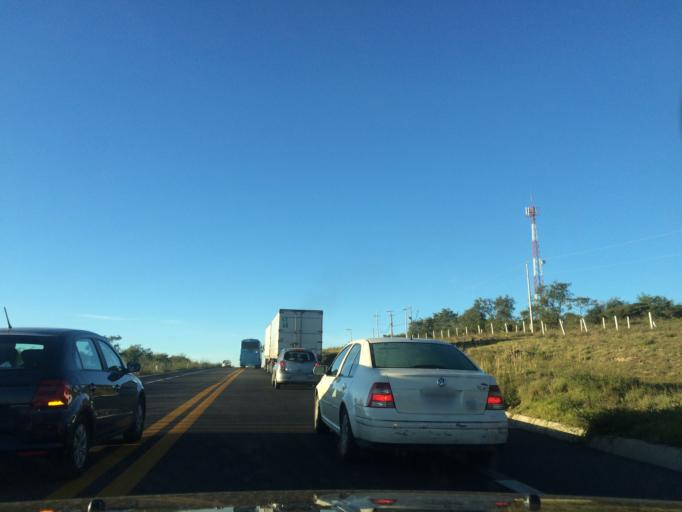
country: MX
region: Puebla
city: Morelos Canada
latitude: 18.7153
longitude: -97.4708
